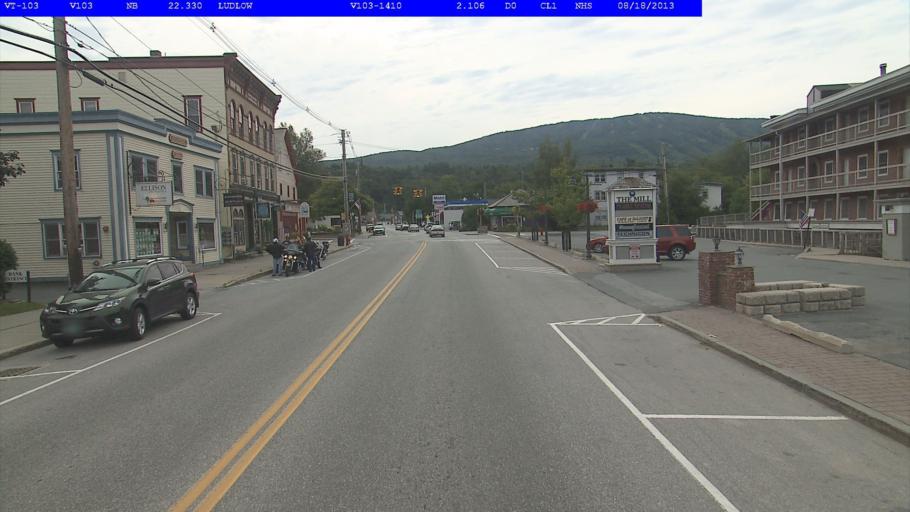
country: US
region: Vermont
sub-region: Windsor County
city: Chester
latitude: 43.3961
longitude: -72.7002
